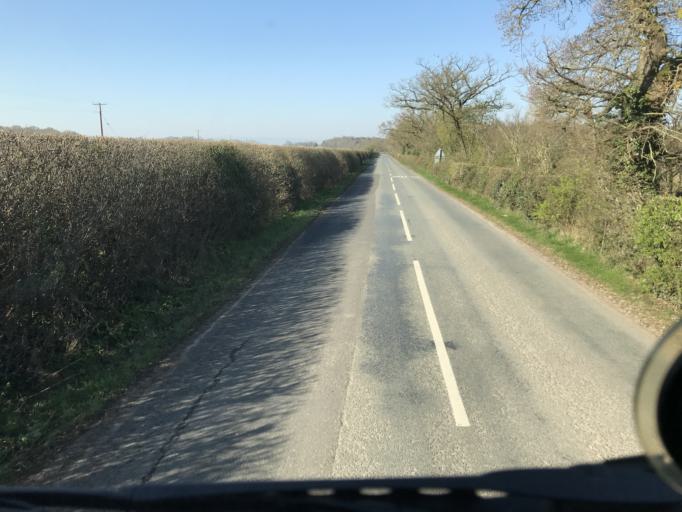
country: GB
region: England
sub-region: Cheshire West and Chester
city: Aldford
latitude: 53.1344
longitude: -2.8474
